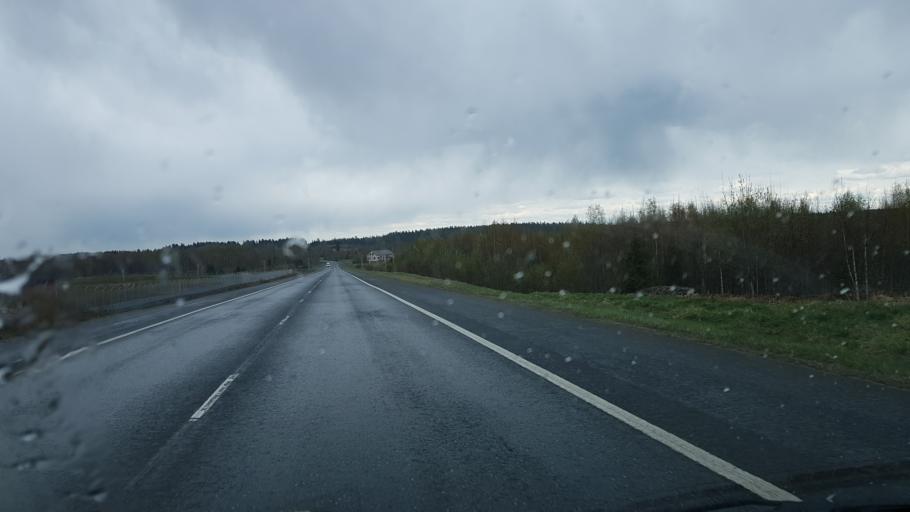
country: FI
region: Pirkanmaa
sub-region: Tampere
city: Pirkkala
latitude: 61.4178
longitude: 23.6344
